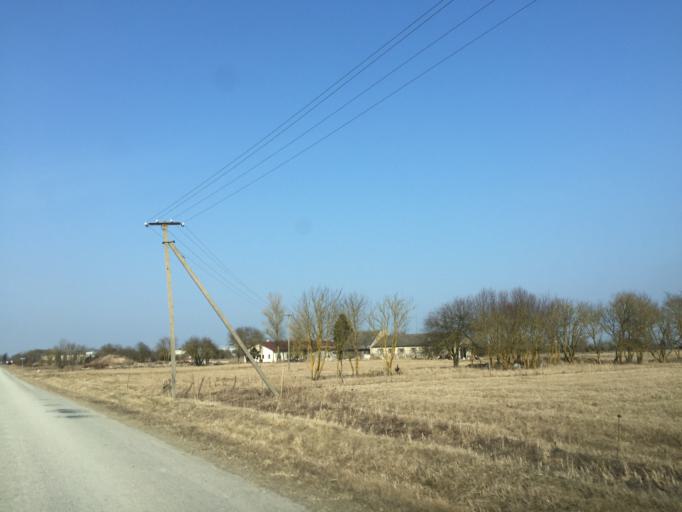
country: EE
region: Saare
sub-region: Orissaare vald
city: Orissaare
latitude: 58.4957
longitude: 23.1160
